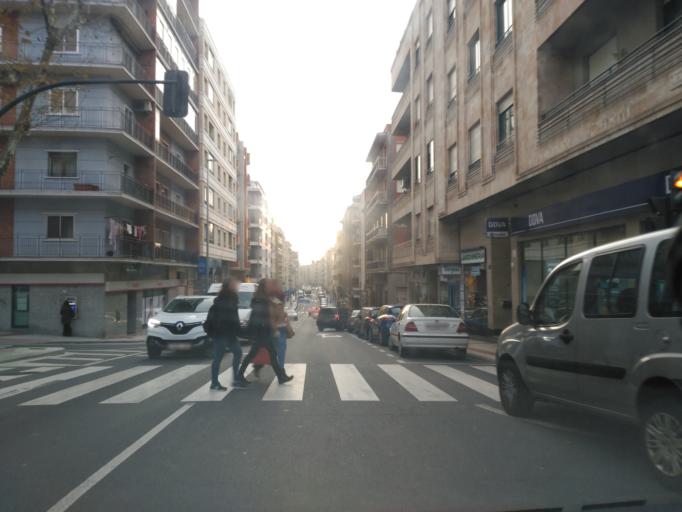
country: ES
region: Castille and Leon
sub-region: Provincia de Salamanca
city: Salamanca
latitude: 40.9728
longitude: -5.6691
